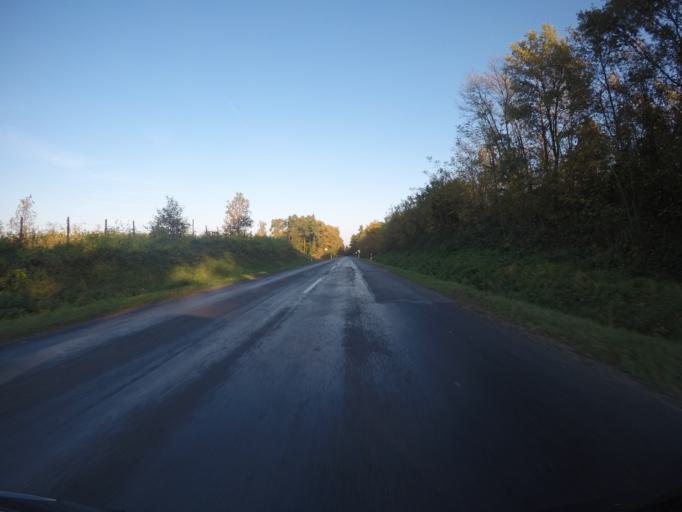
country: HU
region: Somogy
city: Barcs
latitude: 45.9642
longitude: 17.5120
